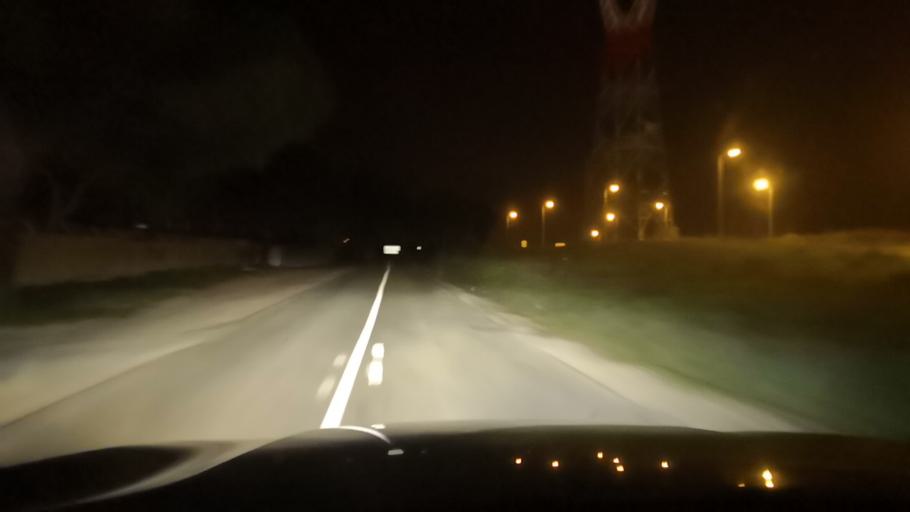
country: PT
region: Setubal
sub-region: Setubal
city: Setubal
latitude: 38.5524
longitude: -8.8635
